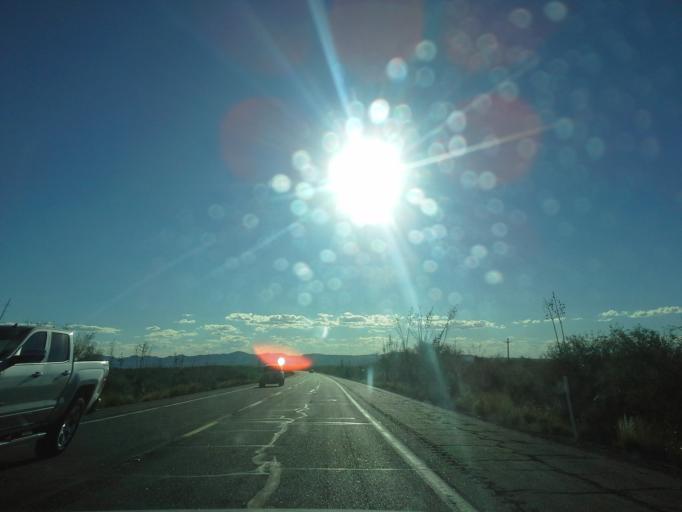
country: US
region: Arizona
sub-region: Pinal County
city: Oracle
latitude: 32.6113
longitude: -110.8437
